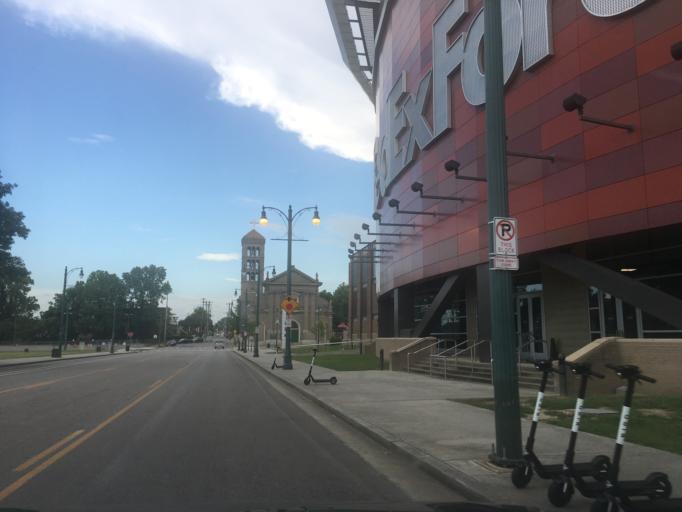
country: US
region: Tennessee
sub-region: Shelby County
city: Memphis
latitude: 35.1385
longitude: -90.0496
